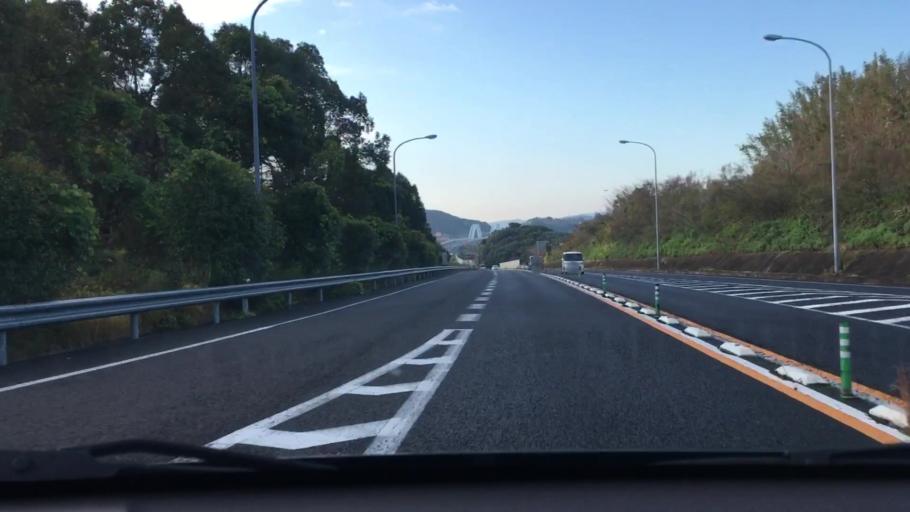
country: JP
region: Nagasaki
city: Sasebo
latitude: 33.0641
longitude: 129.7610
